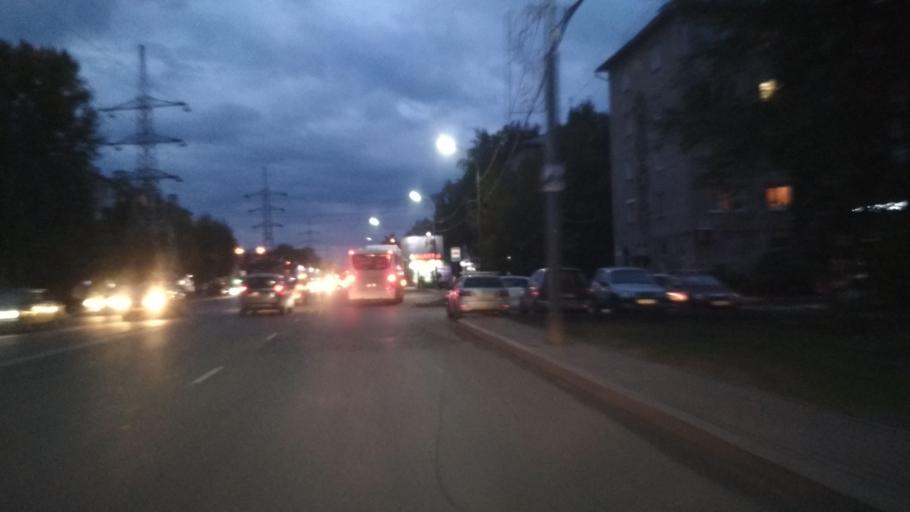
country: RU
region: Tomsk
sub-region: Tomskiy Rayon
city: Tomsk
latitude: 56.4634
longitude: 84.9909
